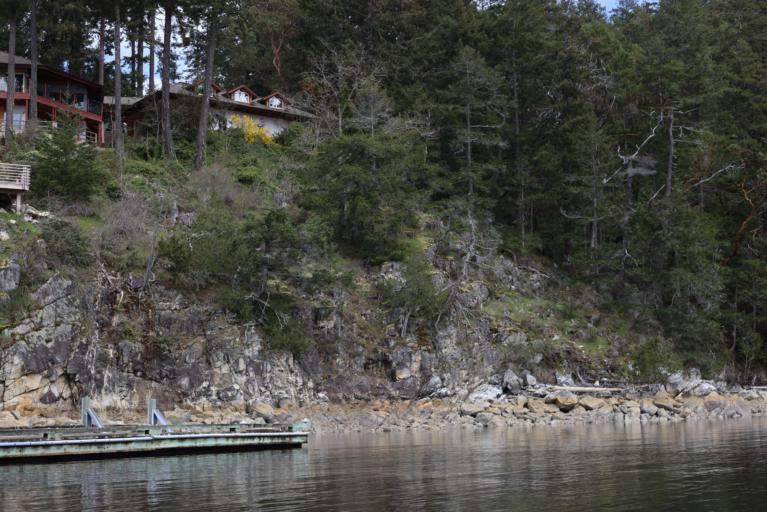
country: CA
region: British Columbia
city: North Saanich
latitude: 48.6054
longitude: -123.4806
